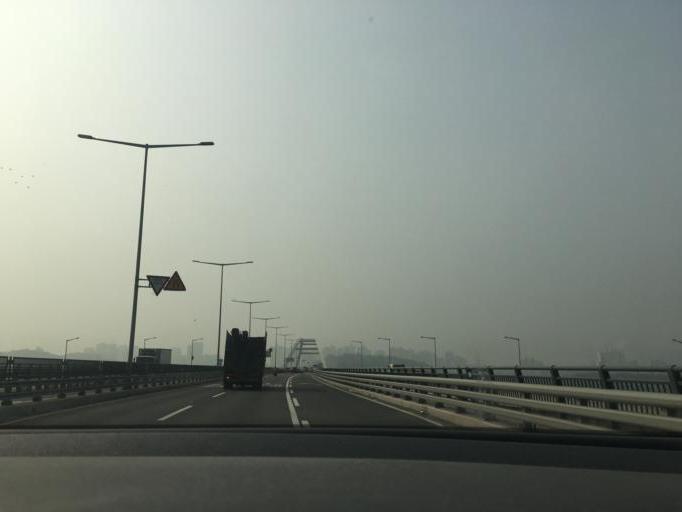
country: KR
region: Gyeonggi-do
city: Guri-si
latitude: 37.5731
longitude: 127.1283
